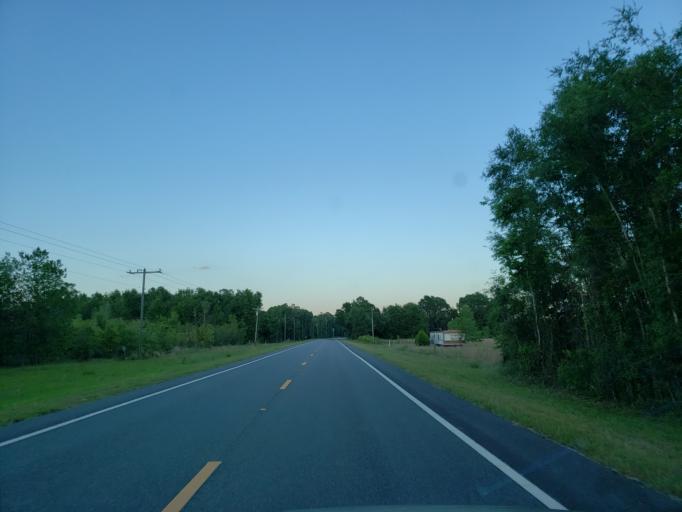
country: US
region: Georgia
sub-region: Echols County
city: Statenville
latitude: 30.5812
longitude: -83.1857
